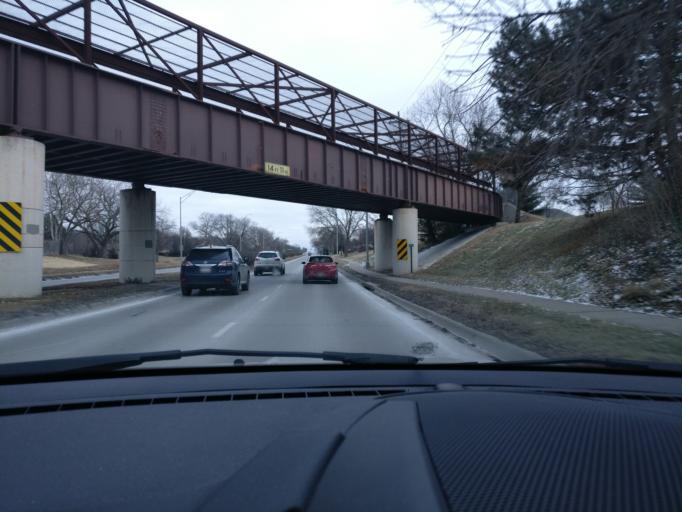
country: US
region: Nebraska
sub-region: Lancaster County
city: Lincoln
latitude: 40.8133
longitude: -96.6212
